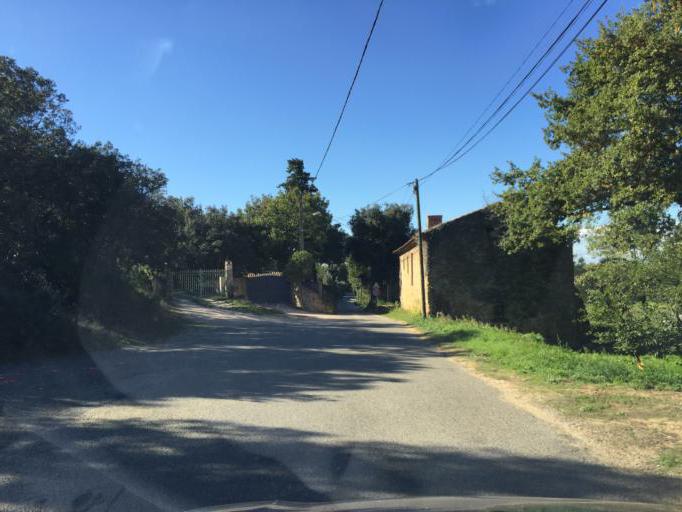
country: FR
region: Provence-Alpes-Cote d'Azur
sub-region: Departement du Vaucluse
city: Piolenc
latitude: 44.1750
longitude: 4.7755
